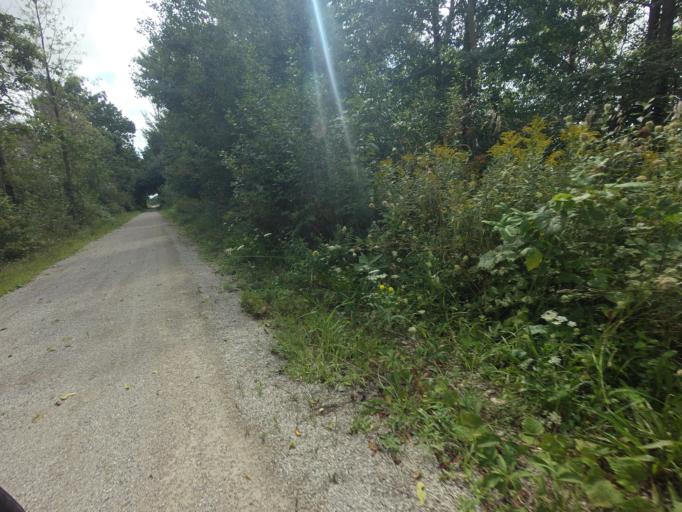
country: CA
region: Ontario
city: Huron East
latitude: 43.6175
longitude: -81.1475
